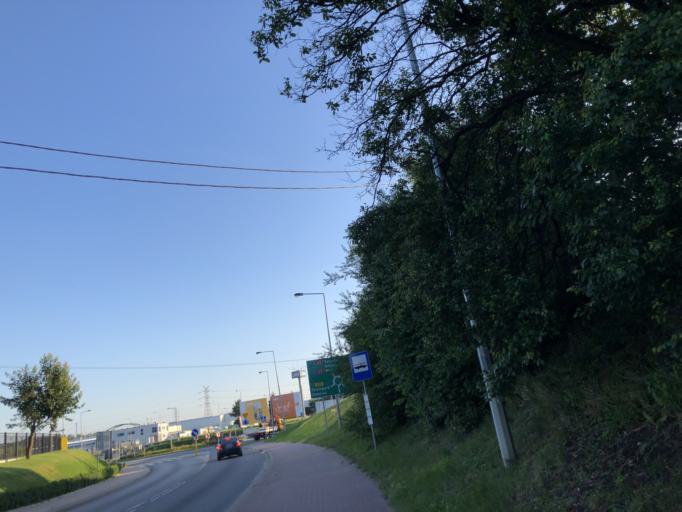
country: PL
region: Pomeranian Voivodeship
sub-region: Powiat gdanski
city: Rotmanka
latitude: 54.2811
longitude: 18.5947
